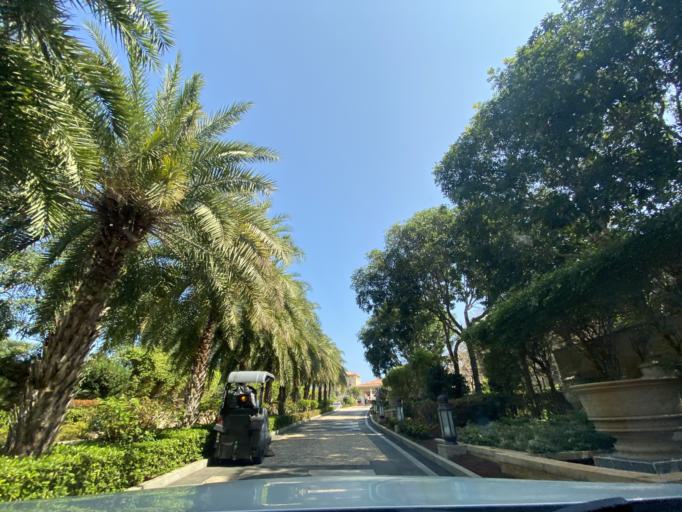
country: CN
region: Hainan
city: Haitangwan
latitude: 18.3507
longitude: 109.7365
